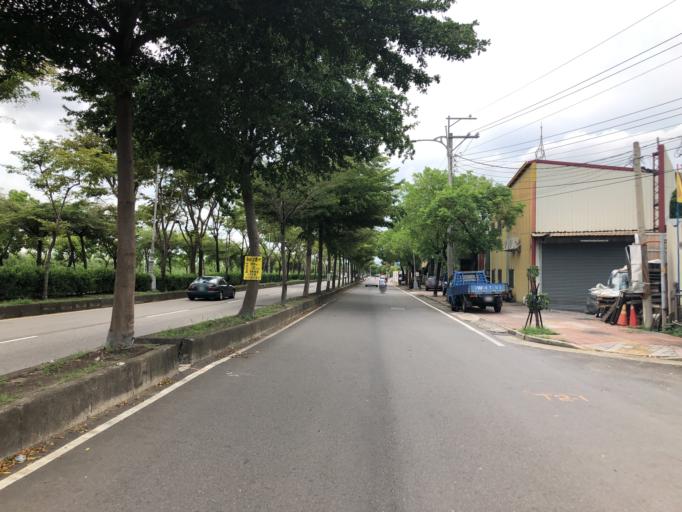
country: TW
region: Taiwan
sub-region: Taichung City
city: Taichung
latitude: 24.0887
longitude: 120.6550
